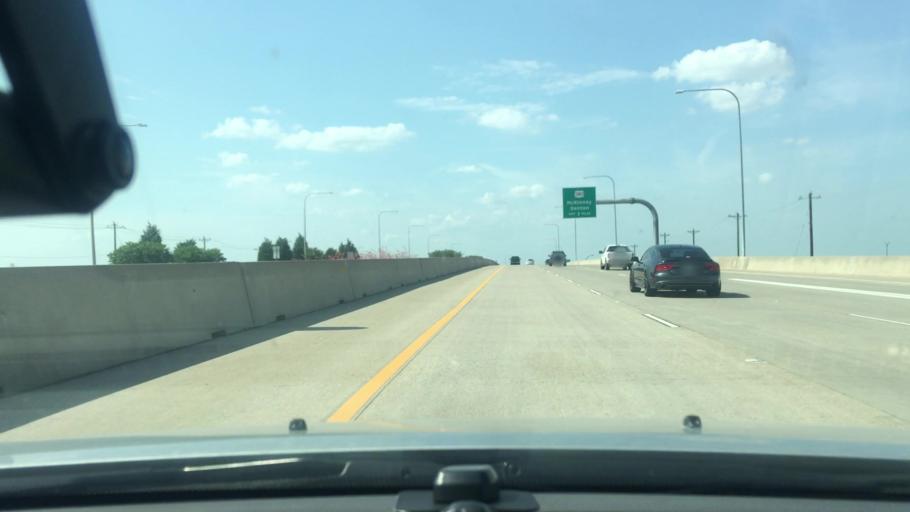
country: US
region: Texas
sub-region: Collin County
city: Frisco
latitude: 33.1875
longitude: -96.8391
